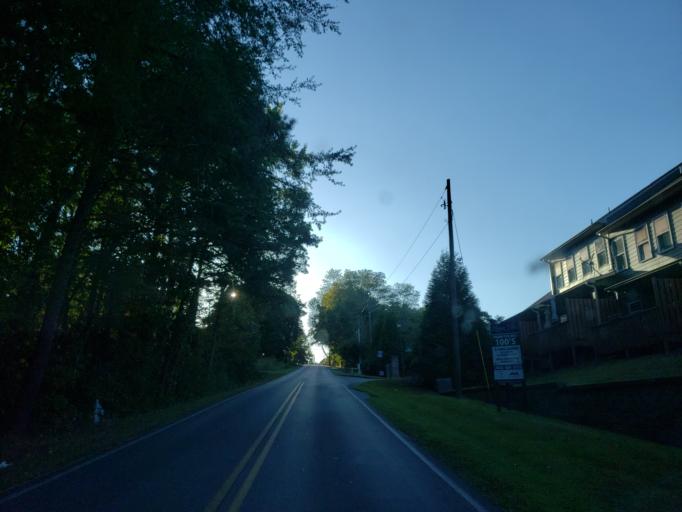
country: US
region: Georgia
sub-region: Pickens County
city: Jasper
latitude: 34.4613
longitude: -84.4183
